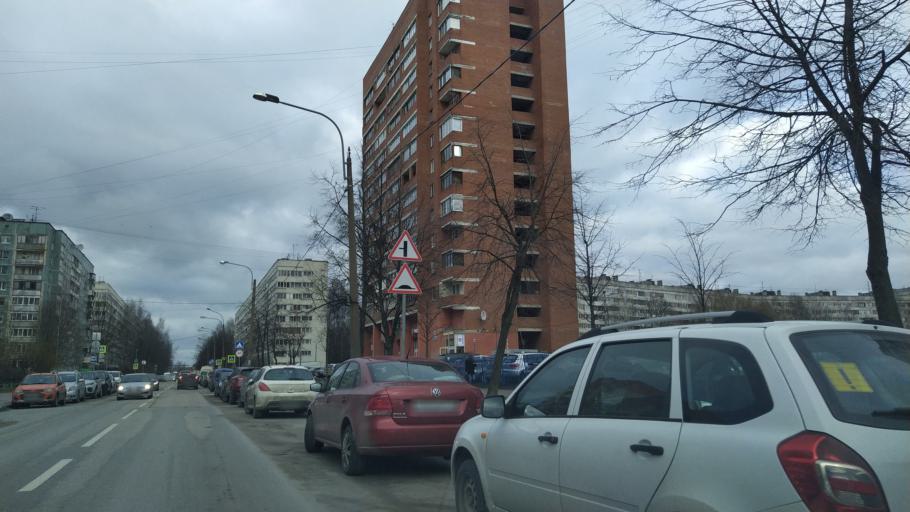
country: RU
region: Leningrad
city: Parnas
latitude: 60.0494
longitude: 30.3691
